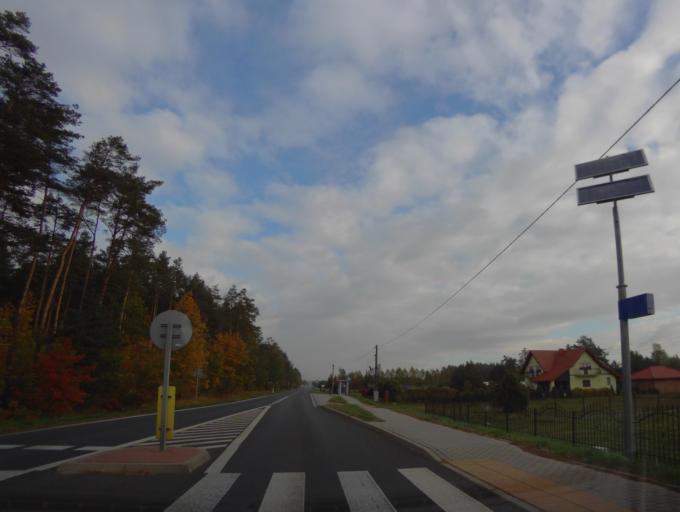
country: PL
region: Lublin Voivodeship
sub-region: Powiat bilgorajski
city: Frampol
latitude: 50.6215
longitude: 22.6826
